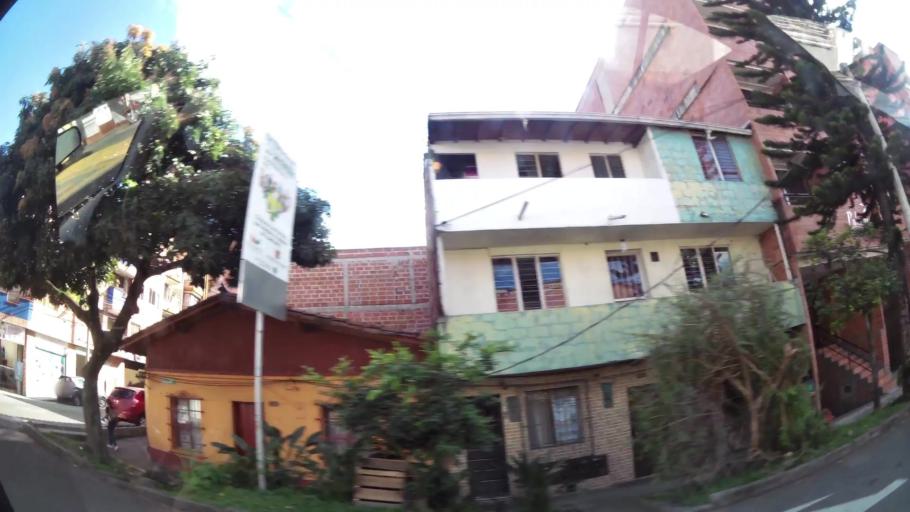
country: CO
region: Antioquia
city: Envigado
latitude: 6.1660
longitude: -75.5817
